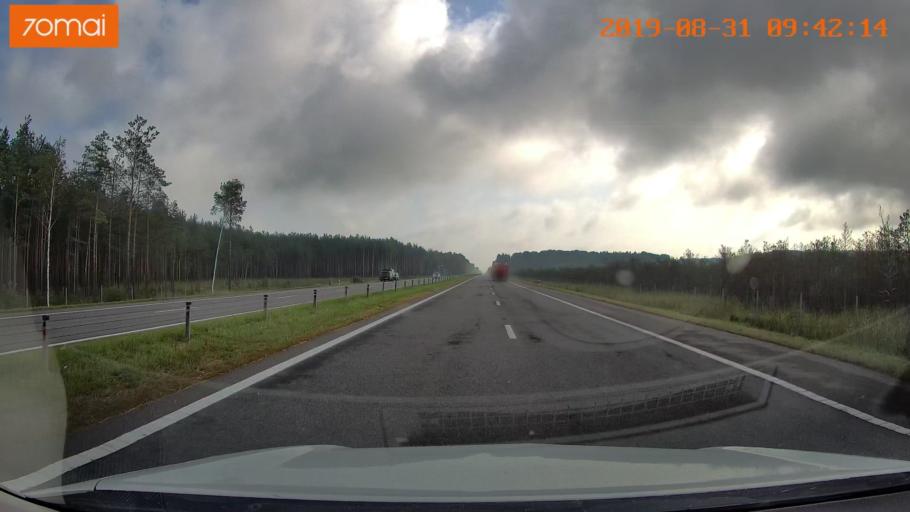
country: BY
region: Mogilev
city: Byalynichy
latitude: 53.9225
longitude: 29.4786
